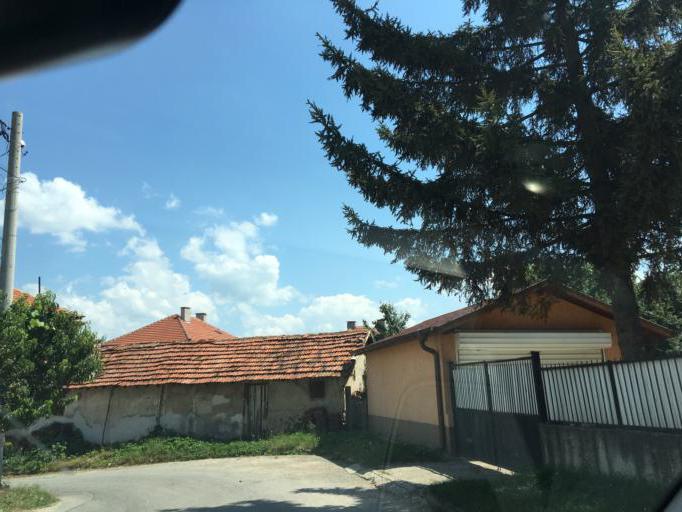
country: BG
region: Sofiya
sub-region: Obshtina Elin Pelin
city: Elin Pelin
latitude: 42.6049
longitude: 23.4714
